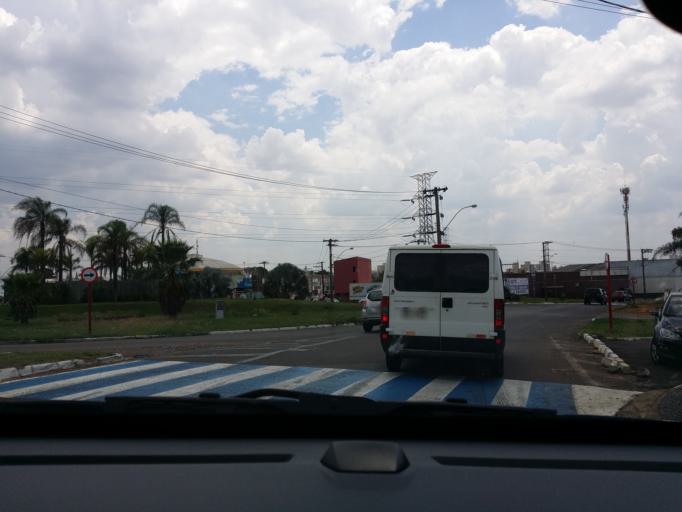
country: BR
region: Sao Paulo
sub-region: Sao Carlos
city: Sao Carlos
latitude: -22.0348
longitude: -47.8710
